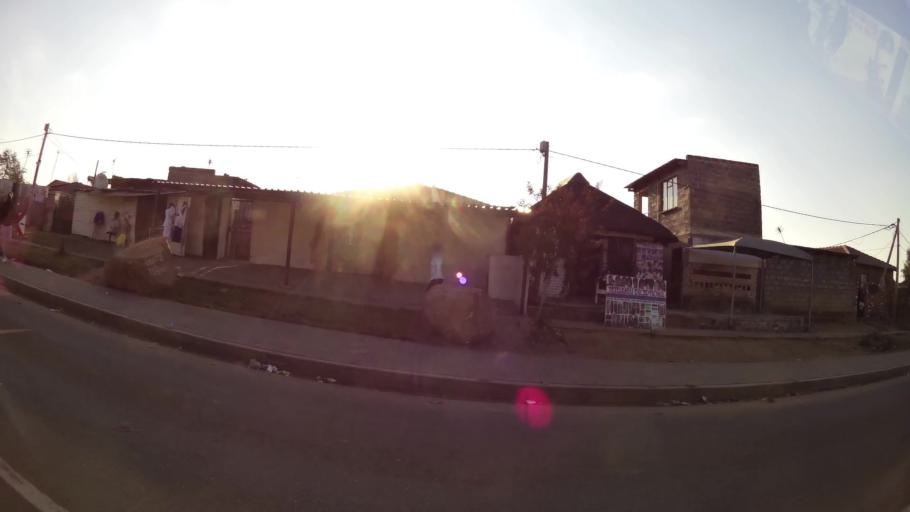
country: ZA
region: Gauteng
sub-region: Ekurhuleni Metropolitan Municipality
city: Tembisa
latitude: -26.0100
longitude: 28.1890
